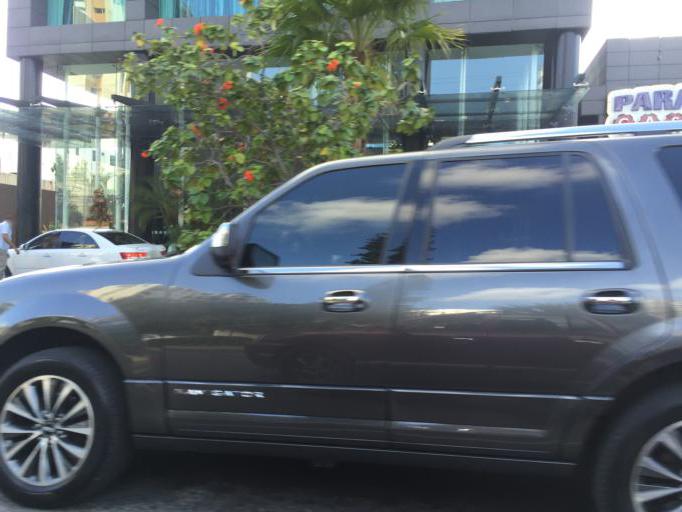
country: DO
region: Nacional
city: La Julia
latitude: 18.4764
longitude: -69.9365
